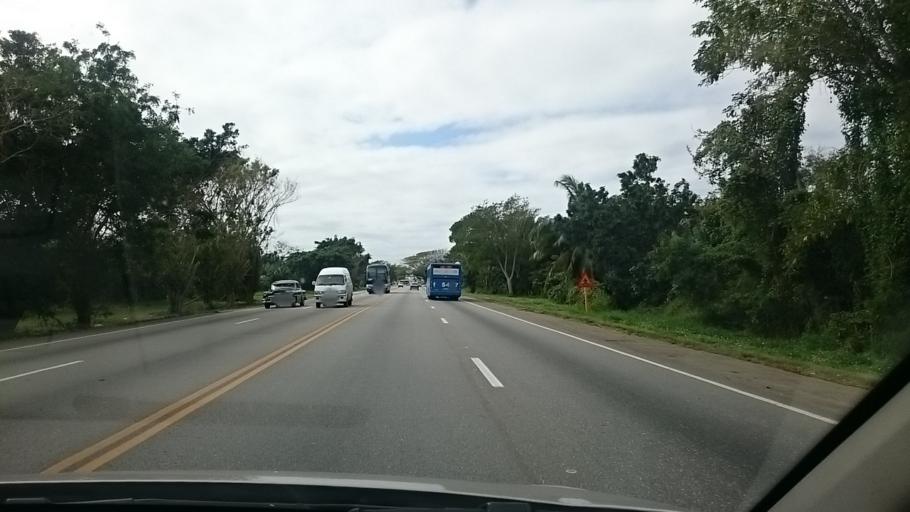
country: CU
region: La Habana
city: Alamar
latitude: 23.1588
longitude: -82.2672
